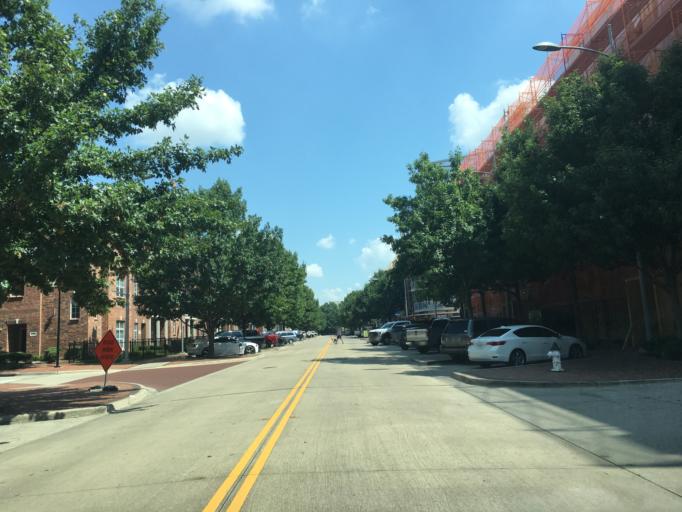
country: US
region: Texas
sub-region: Dallas County
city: Addison
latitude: 32.9635
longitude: -96.8240
